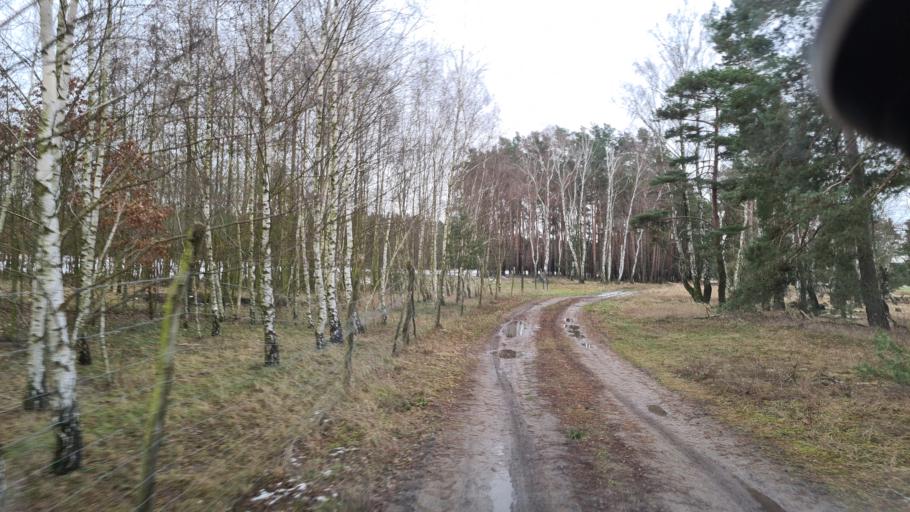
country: DE
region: Brandenburg
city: Schenkendobern
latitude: 51.9101
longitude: 14.5909
